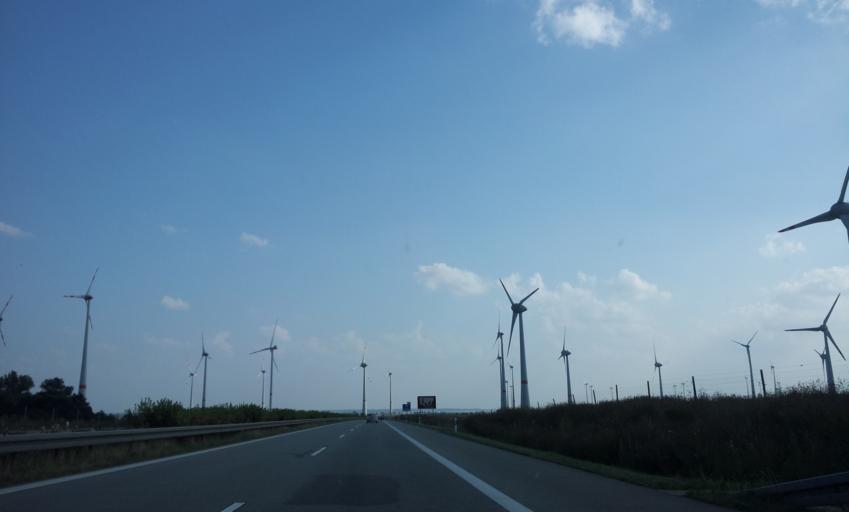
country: DE
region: Mecklenburg-Vorpommern
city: Kessin
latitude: 53.7317
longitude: 13.3343
